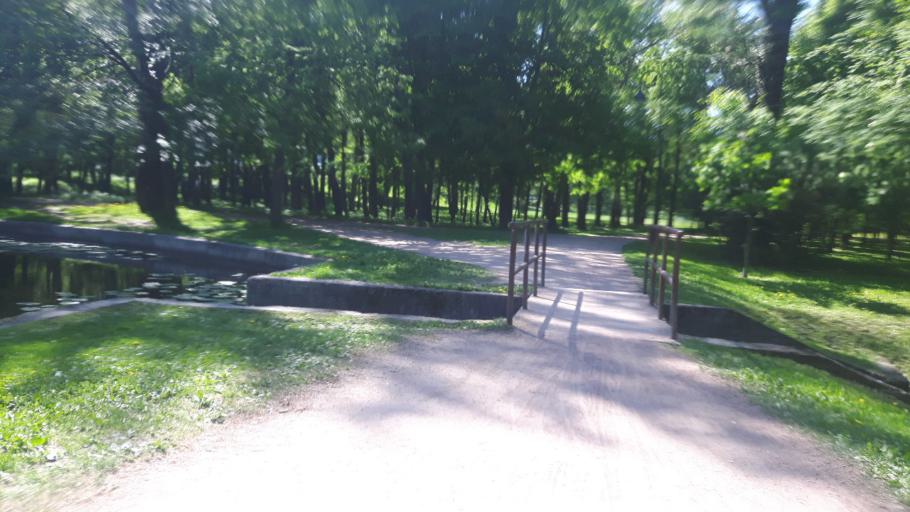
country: RU
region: St.-Petersburg
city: Sosnovaya Polyana
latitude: 59.8468
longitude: 30.1347
